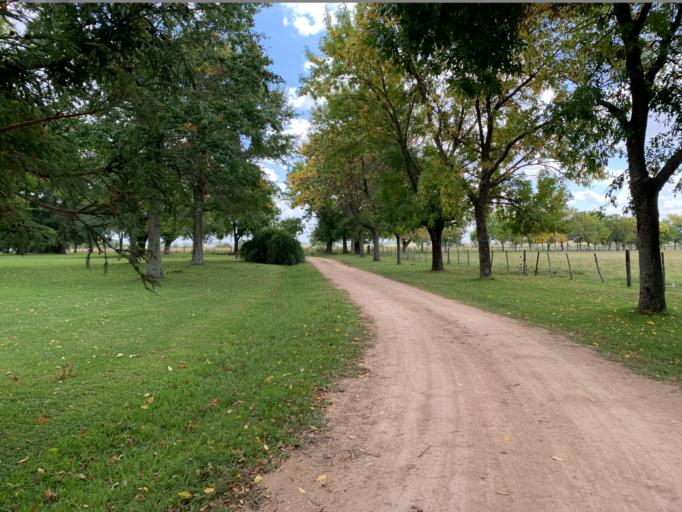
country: AR
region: Buenos Aires
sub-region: San Antonio de Areco
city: San Antonio de Areco
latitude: -34.1963
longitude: -59.3876
